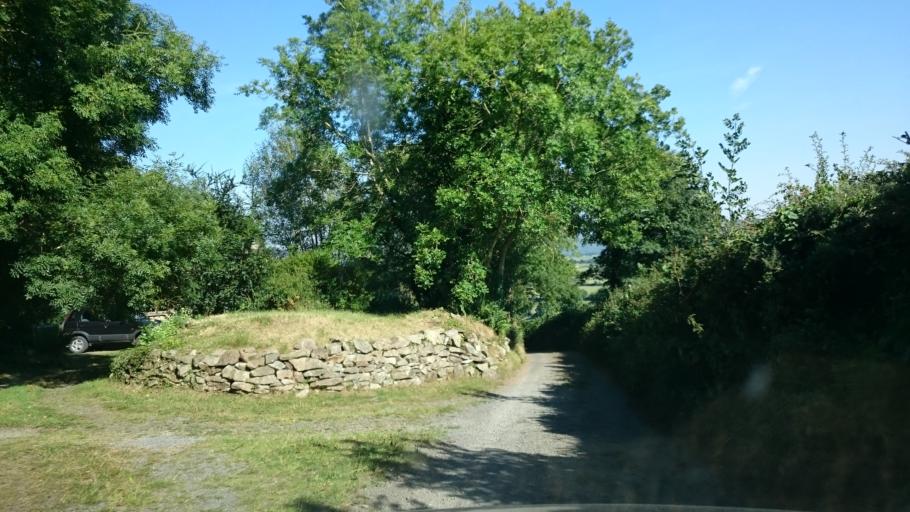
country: IE
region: Leinster
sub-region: Kilkenny
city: Graiguenamanagh
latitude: 52.5286
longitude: -6.9596
